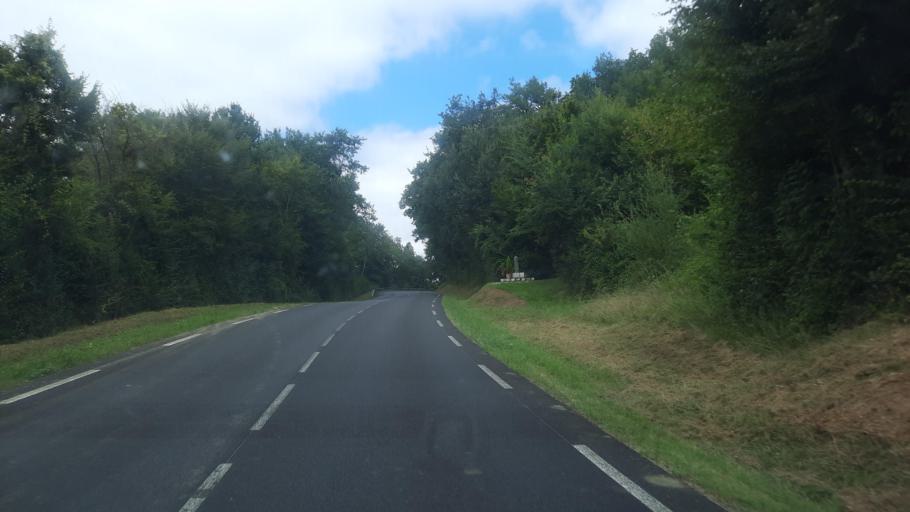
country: FR
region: Midi-Pyrenees
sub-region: Departement des Hautes-Pyrenees
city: Orleix
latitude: 43.2796
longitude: 0.1901
